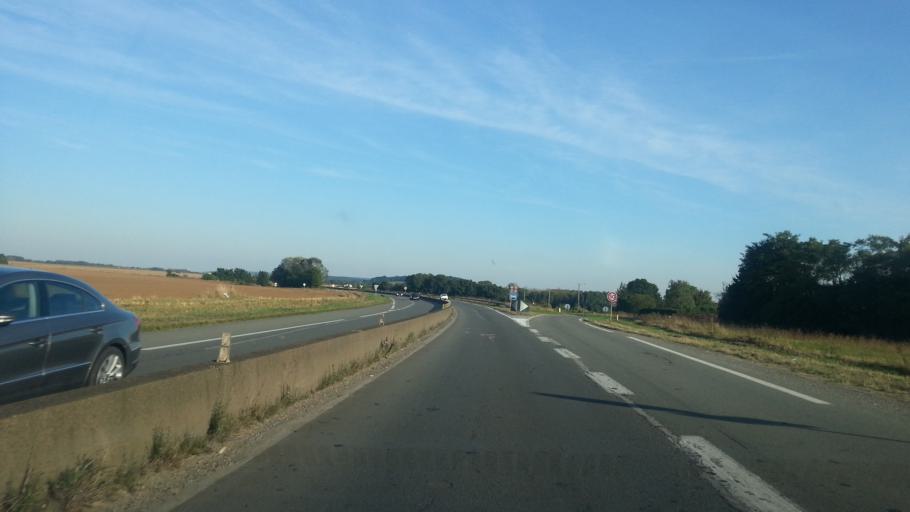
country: FR
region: Picardie
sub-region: Departement de l'Oise
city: Allonne
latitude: 49.4272
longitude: 2.1297
